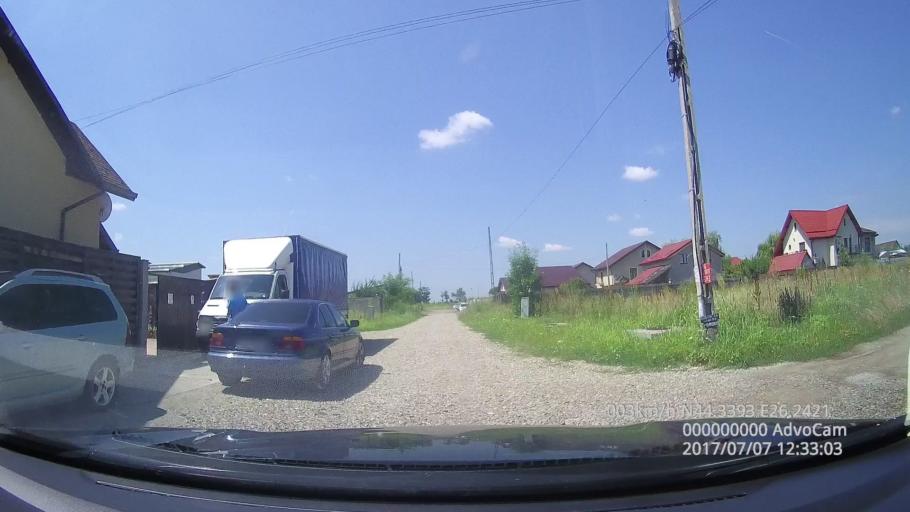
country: RO
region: Ilfov
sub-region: Comuna Glina
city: Glina
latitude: 44.3393
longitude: 26.2421
